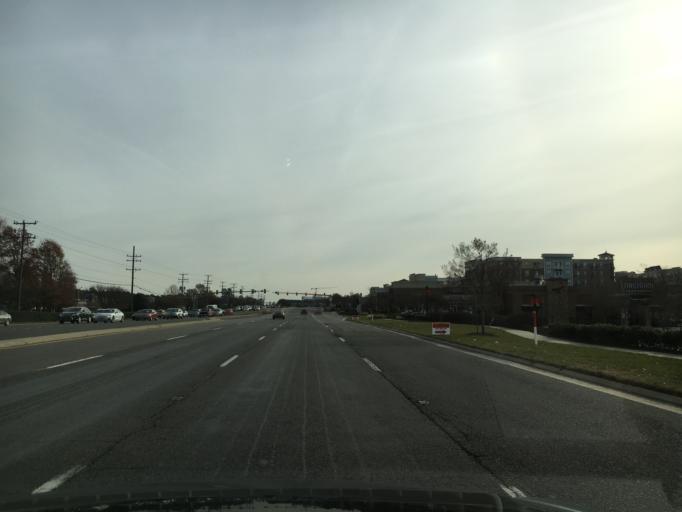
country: US
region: Virginia
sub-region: Henrico County
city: Short Pump
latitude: 37.6502
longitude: -77.6067
